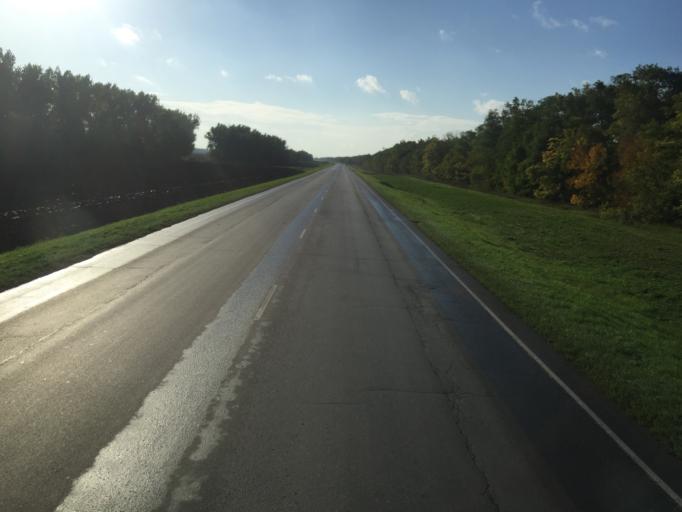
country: RU
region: Rostov
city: Yegorlykskaya
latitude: 46.6309
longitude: 40.5879
